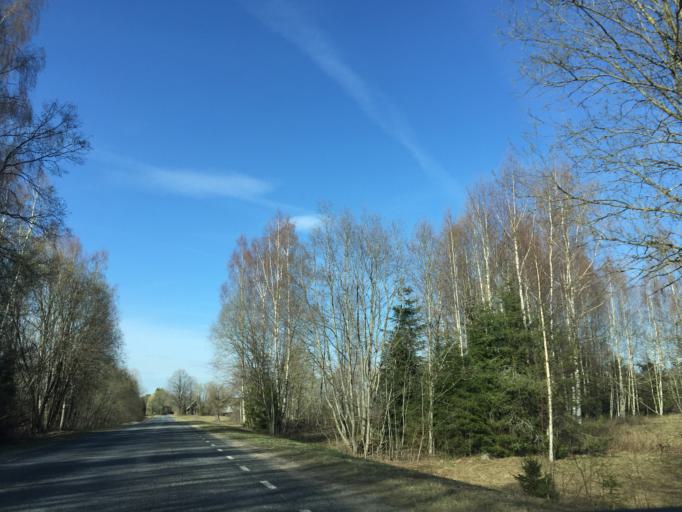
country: EE
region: Vorumaa
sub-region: Antsla vald
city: Vana-Antsla
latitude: 57.9844
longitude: 26.4094
